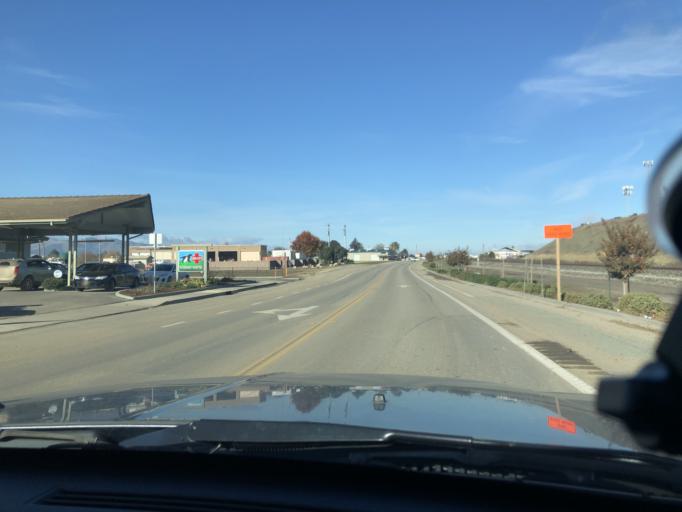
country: US
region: California
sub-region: Monterey County
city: King City
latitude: 36.2034
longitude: -121.1136
